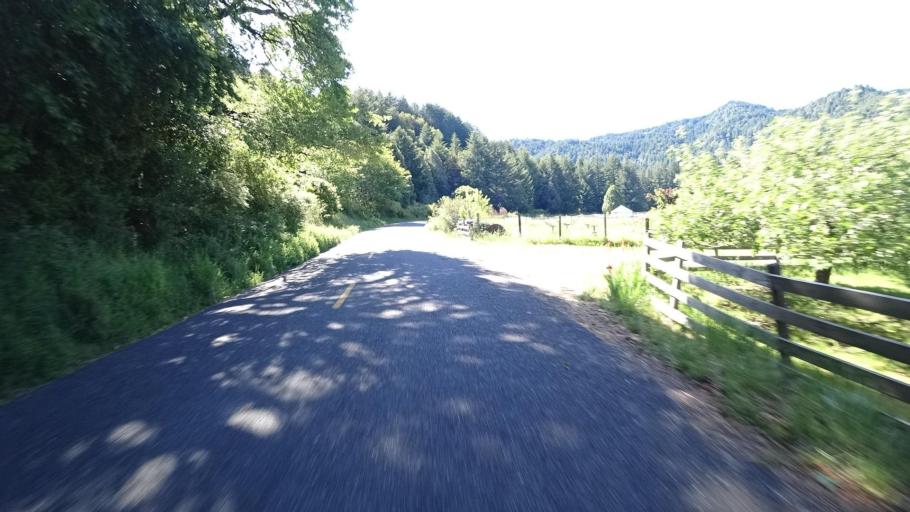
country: US
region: California
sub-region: Humboldt County
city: Rio Dell
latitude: 40.2733
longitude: -124.2308
